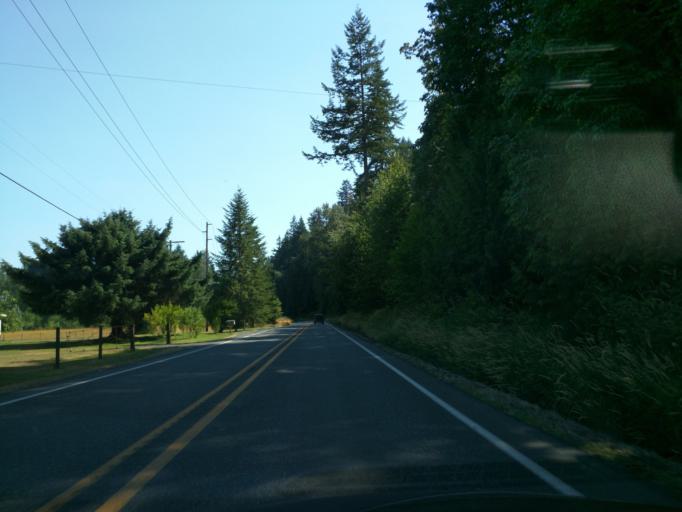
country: US
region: Washington
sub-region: Whatcom County
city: Peaceful Valley
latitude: 48.8641
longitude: -122.1531
